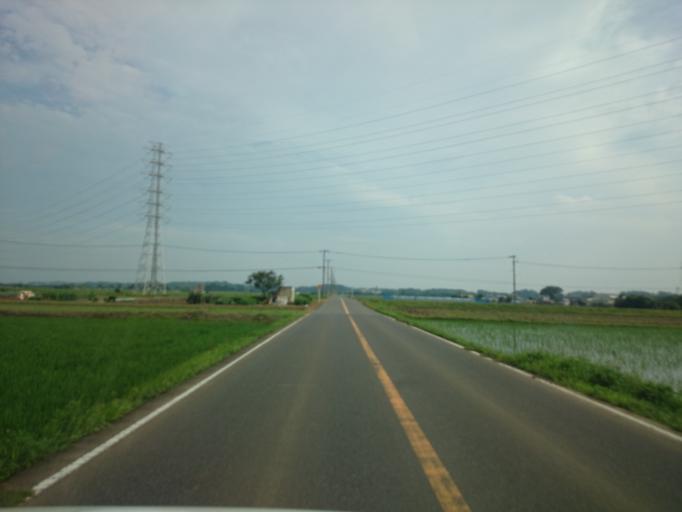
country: JP
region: Ibaraki
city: Tsukuba
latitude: 36.1531
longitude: 140.0992
